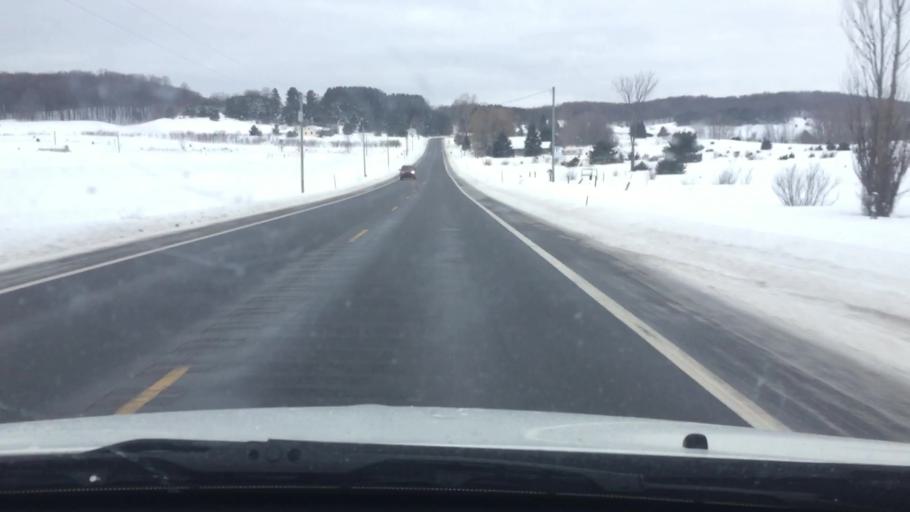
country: US
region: Michigan
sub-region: Charlevoix County
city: East Jordan
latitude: 45.1035
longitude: -85.0411
